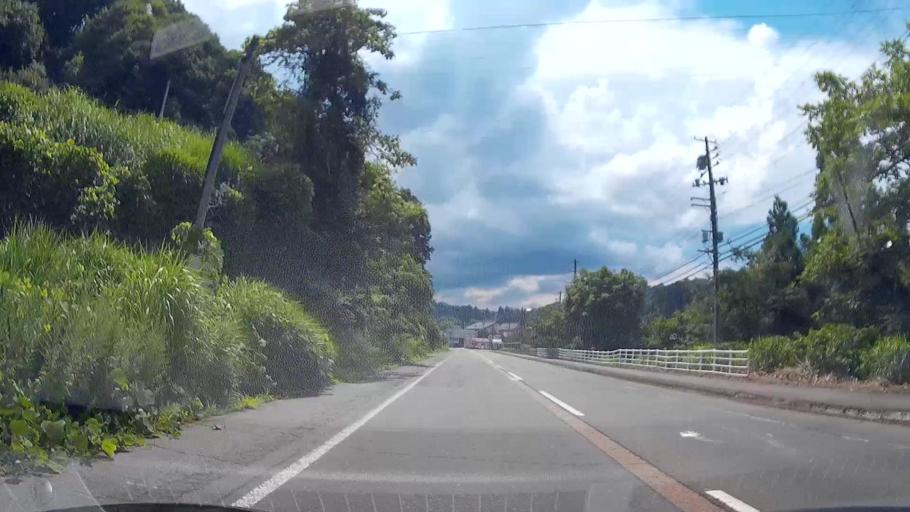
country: JP
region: Niigata
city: Tokamachi
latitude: 36.9934
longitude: 138.5925
